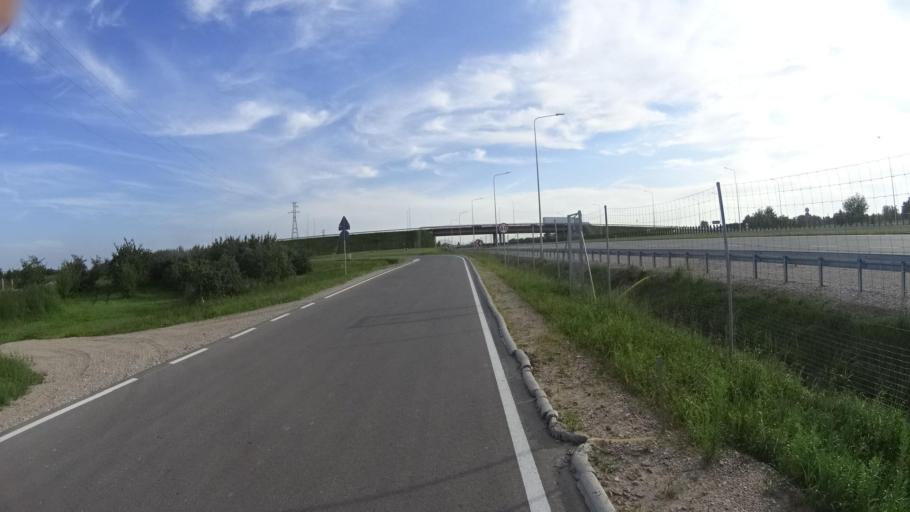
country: PL
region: Masovian Voivodeship
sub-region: Powiat piaseczynski
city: Tarczyn
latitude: 51.9529
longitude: 20.8467
